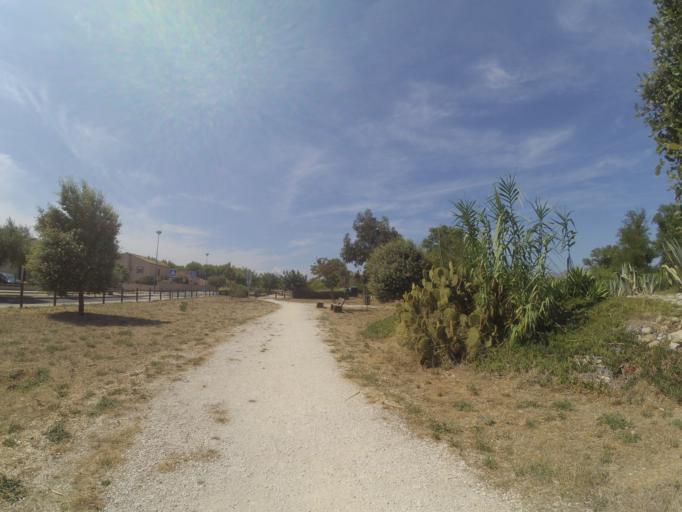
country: FR
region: Languedoc-Roussillon
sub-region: Departement des Pyrenees-Orientales
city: Peyrestortes
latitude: 42.7553
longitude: 2.8504
